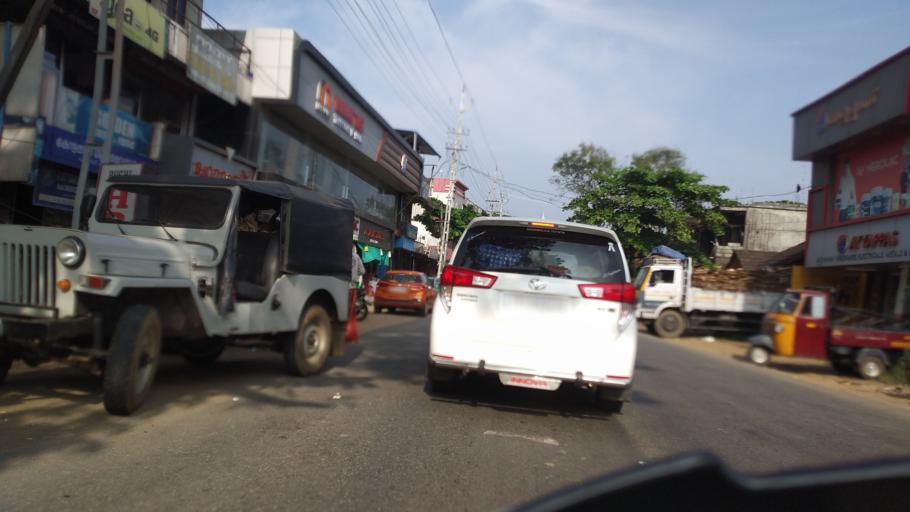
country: IN
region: Kerala
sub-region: Thrissur District
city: Chelakara
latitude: 10.5891
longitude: 76.5149
